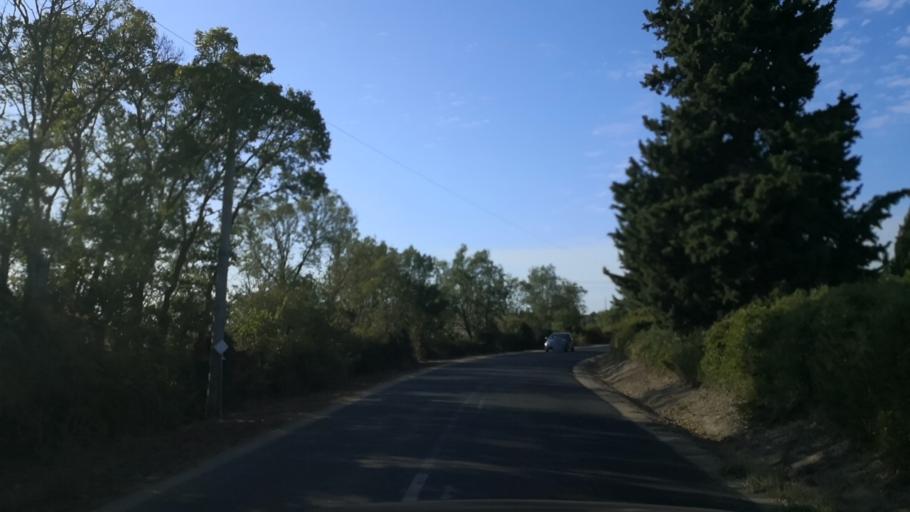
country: PT
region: Santarem
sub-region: Santarem
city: Santarem
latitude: 39.2694
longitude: -8.6627
